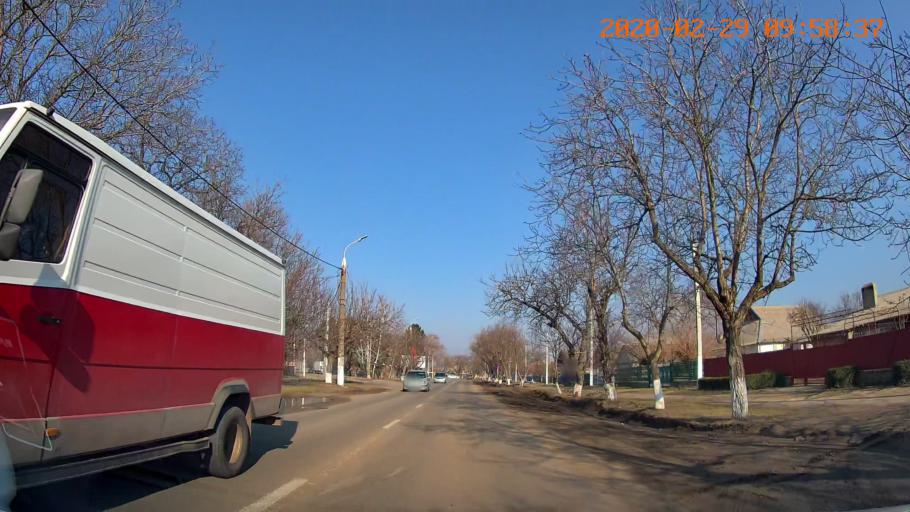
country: MD
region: Telenesti
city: Slobozia
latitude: 46.7503
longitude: 29.6906
